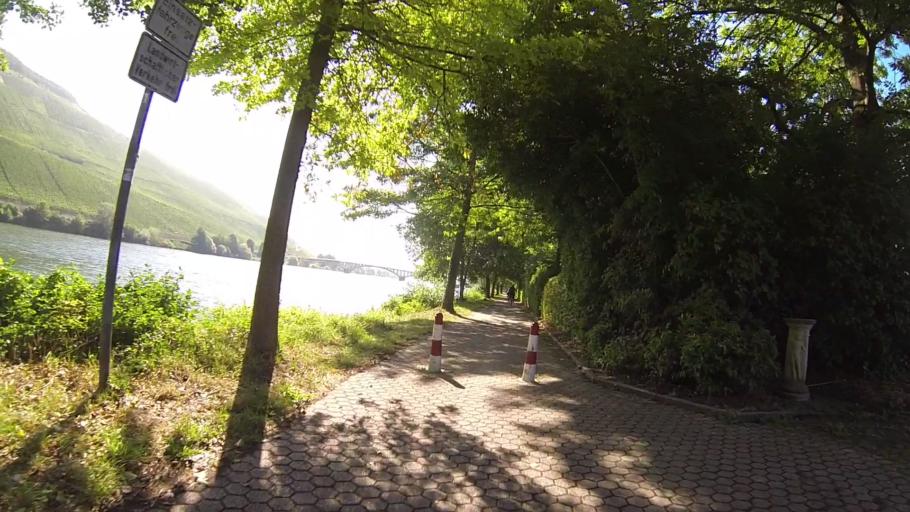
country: DE
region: Rheinland-Pfalz
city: Longuich
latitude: 49.8091
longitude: 6.7735
